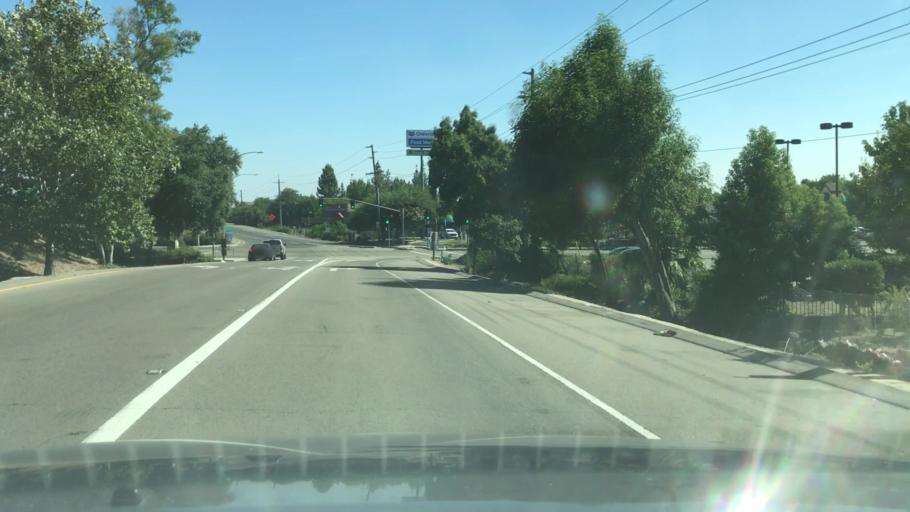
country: US
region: California
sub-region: San Joaquin County
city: Lincoln Village
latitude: 38.0222
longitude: -121.3598
